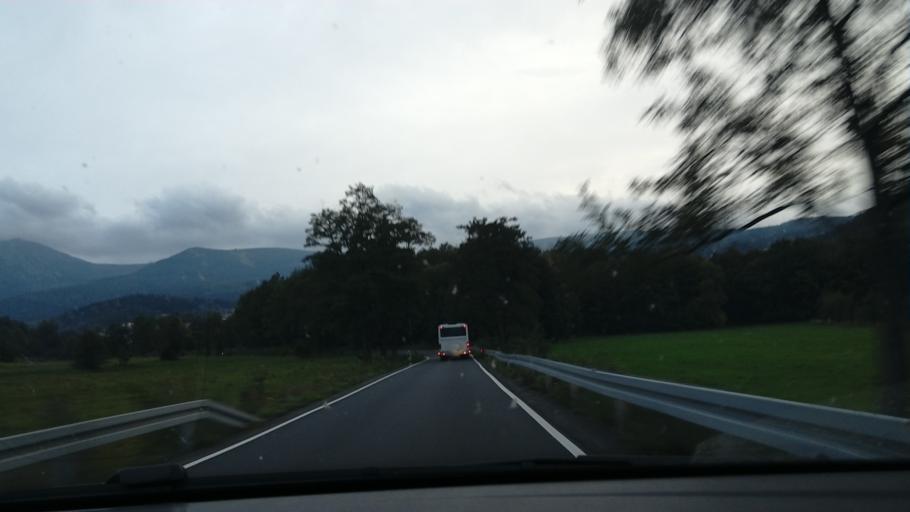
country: PL
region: Lower Silesian Voivodeship
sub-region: Powiat jeleniogorski
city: Karpacz
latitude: 50.7876
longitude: 15.7691
